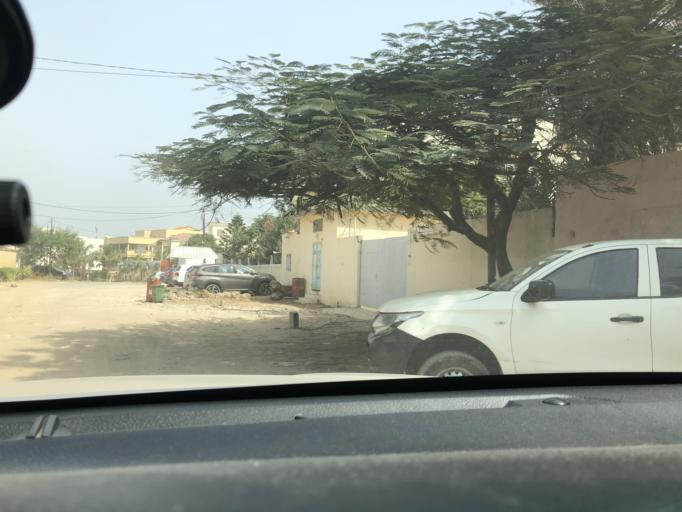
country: SN
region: Dakar
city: Mermoz Boabab
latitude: 14.7407
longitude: -17.5147
